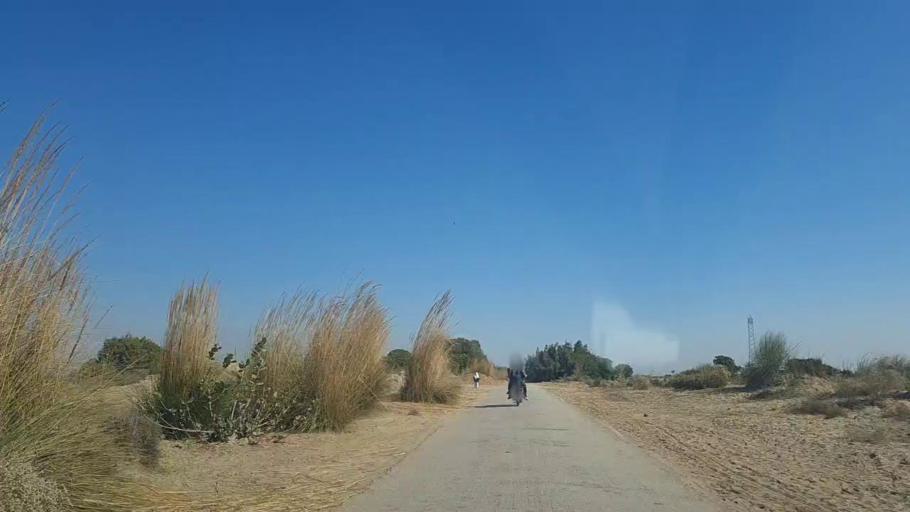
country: PK
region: Sindh
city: Khadro
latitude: 26.2094
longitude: 68.8273
